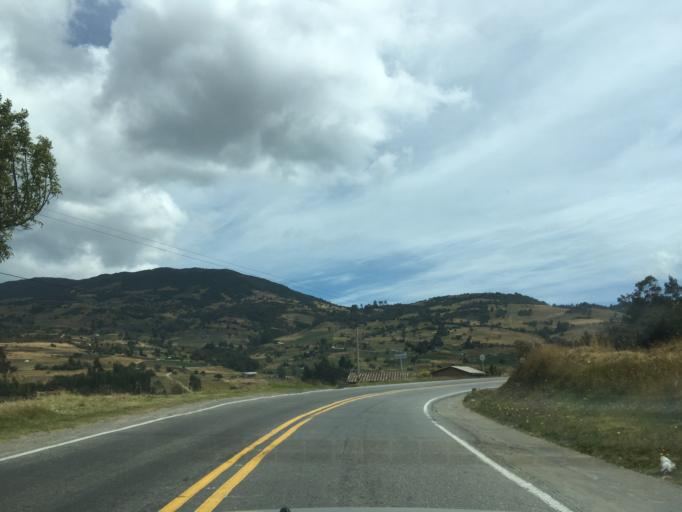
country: CO
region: Boyaca
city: Firavitoba
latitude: 5.6222
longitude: -72.9115
